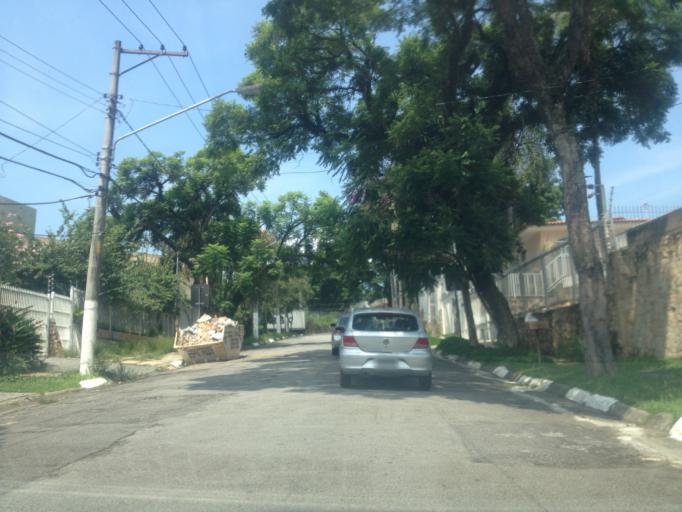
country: BR
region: Sao Paulo
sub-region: Diadema
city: Diadema
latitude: -23.6513
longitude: -46.6796
